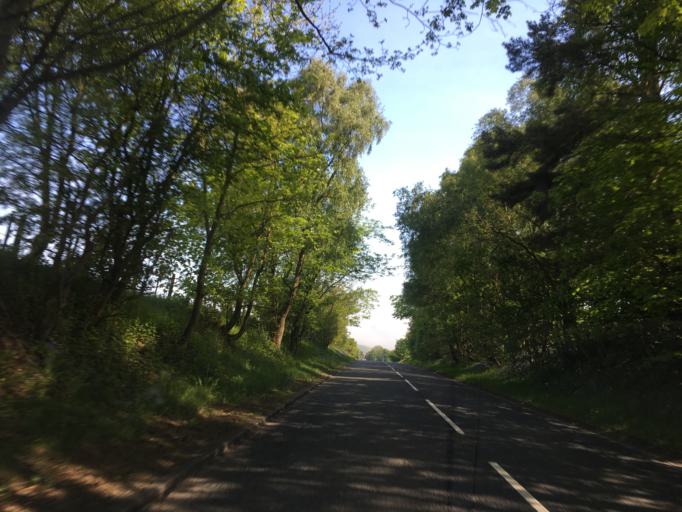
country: GB
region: Scotland
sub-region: The Scottish Borders
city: West Linton
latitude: 55.6806
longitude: -3.4016
